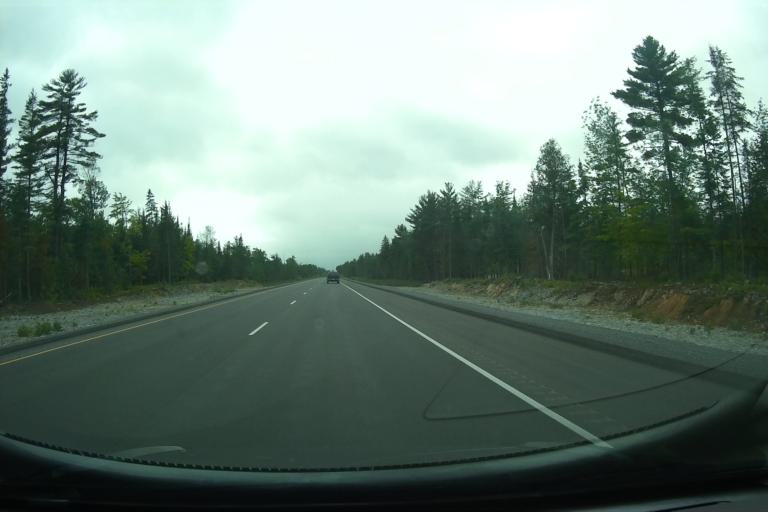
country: CA
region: Ontario
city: Arnprior
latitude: 45.4371
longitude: -76.4347
